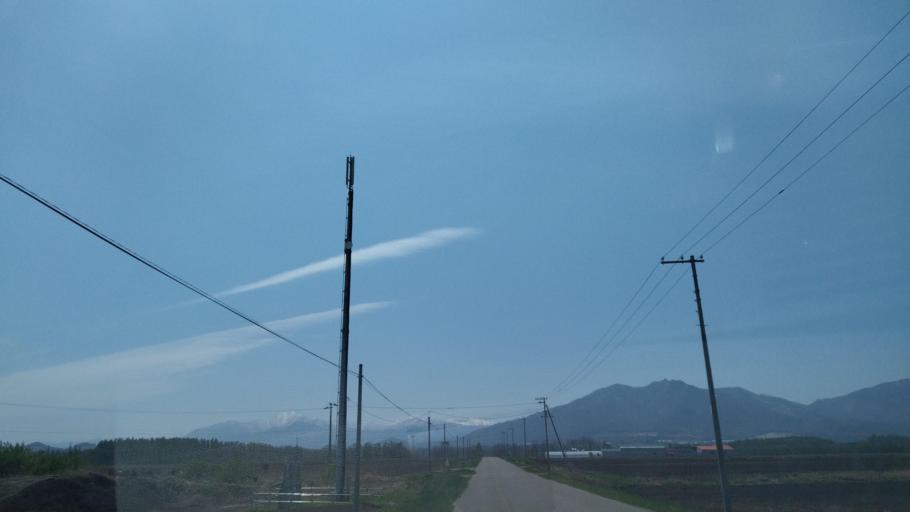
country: JP
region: Hokkaido
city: Obihiro
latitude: 42.9021
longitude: 142.9842
